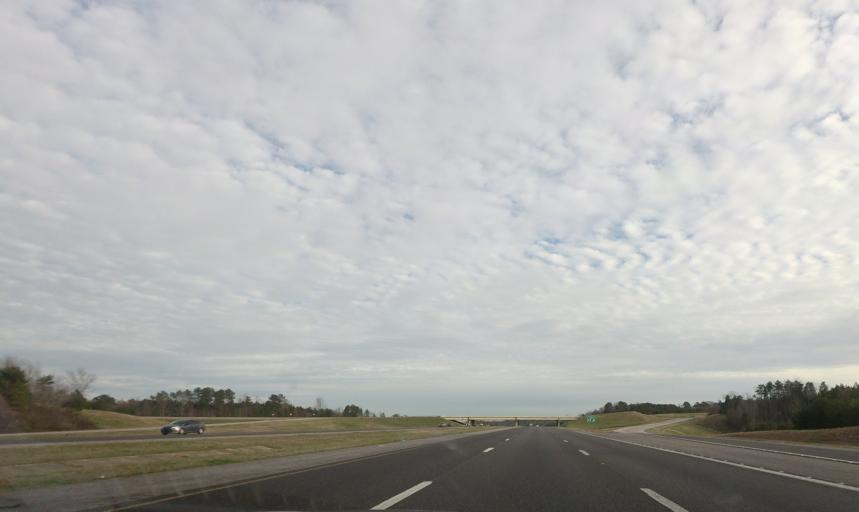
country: US
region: Alabama
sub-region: Jefferson County
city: Adamsville
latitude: 33.6130
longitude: -86.9325
